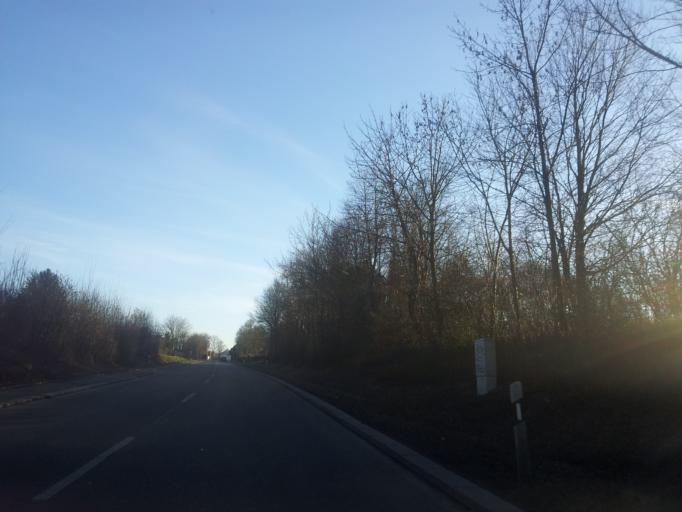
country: DE
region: Baden-Wuerttemberg
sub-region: Regierungsbezirk Stuttgart
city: Flein
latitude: 49.1141
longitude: 9.2139
